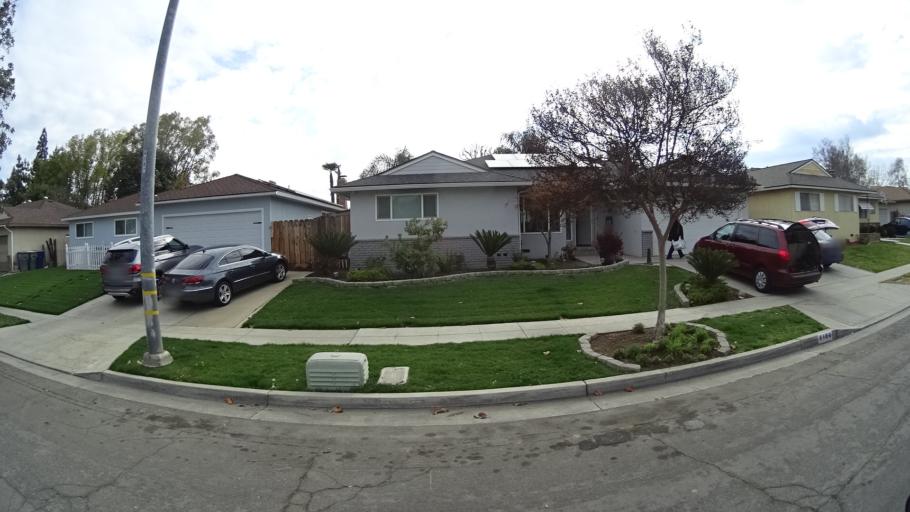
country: US
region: California
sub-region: Fresno County
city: Clovis
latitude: 36.8269
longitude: -119.7643
